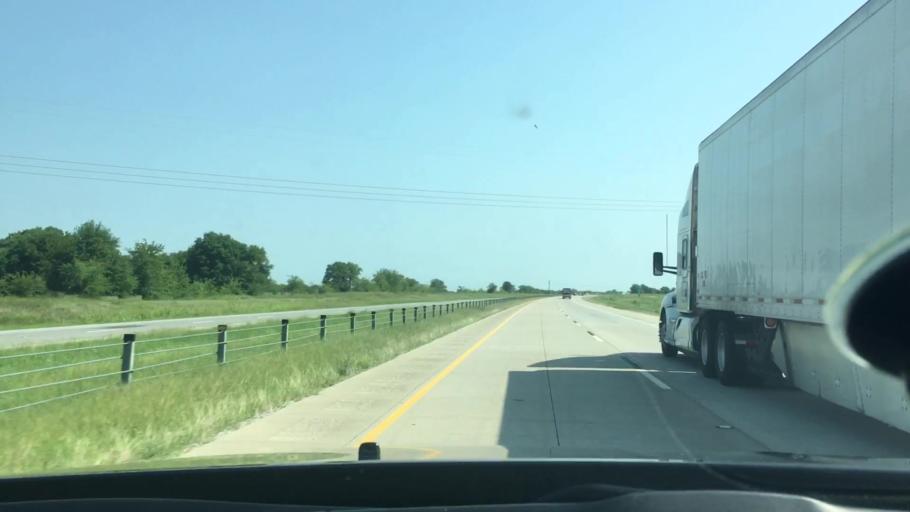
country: US
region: Oklahoma
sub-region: Bryan County
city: Durant
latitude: 34.0786
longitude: -96.3370
